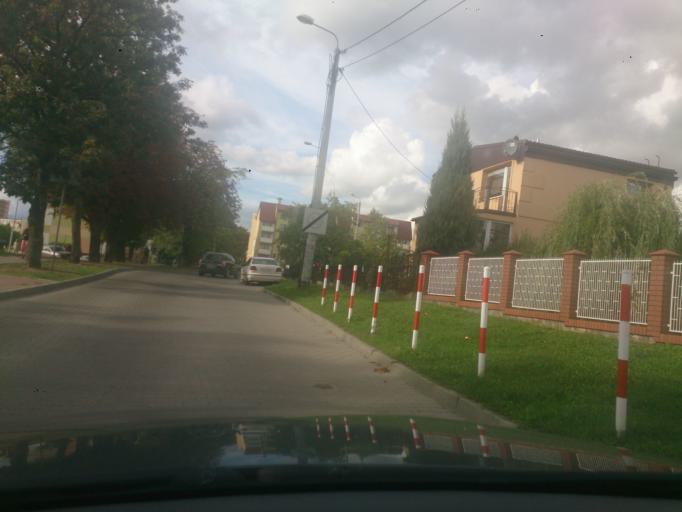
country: PL
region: Kujawsko-Pomorskie
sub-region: Grudziadz
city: Grudziadz
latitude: 53.4632
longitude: 18.7322
